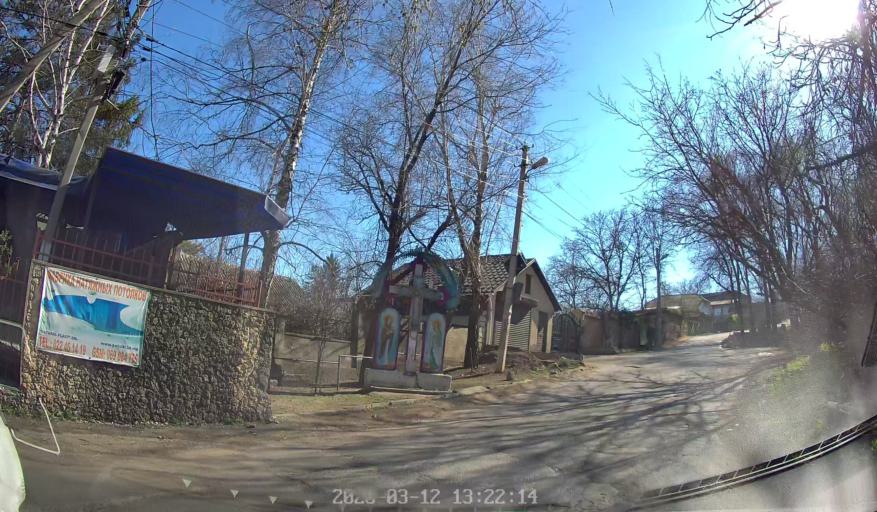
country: MD
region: Laloveni
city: Ialoveni
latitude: 46.9475
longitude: 28.8367
